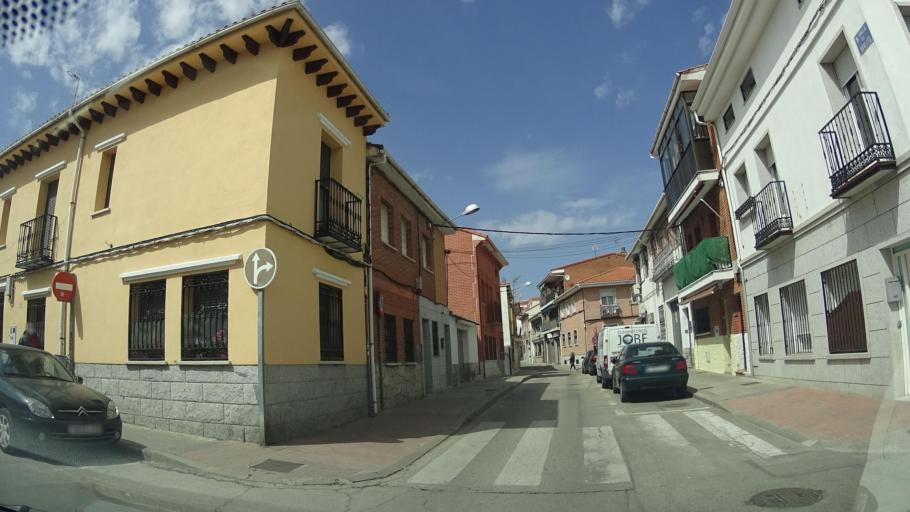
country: ES
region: Madrid
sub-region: Provincia de Madrid
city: Colmenar Viejo
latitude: 40.6613
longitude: -3.7704
